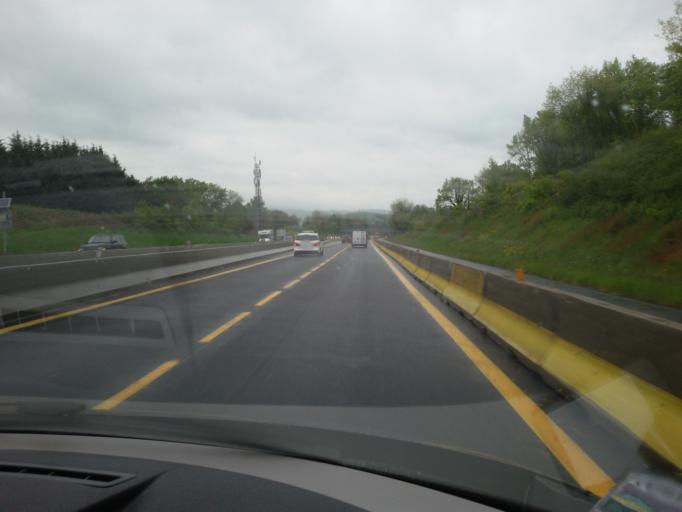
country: FR
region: Rhone-Alpes
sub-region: Departement du Rhone
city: Limonest
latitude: 45.8417
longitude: 4.7521
